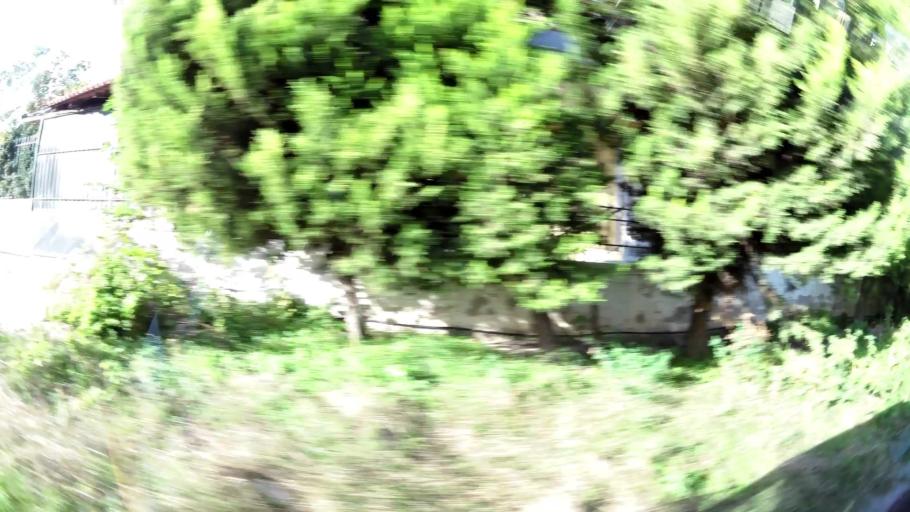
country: GR
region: Attica
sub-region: Nomarchia Anatolikis Attikis
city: Acharnes
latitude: 38.0691
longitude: 23.7451
